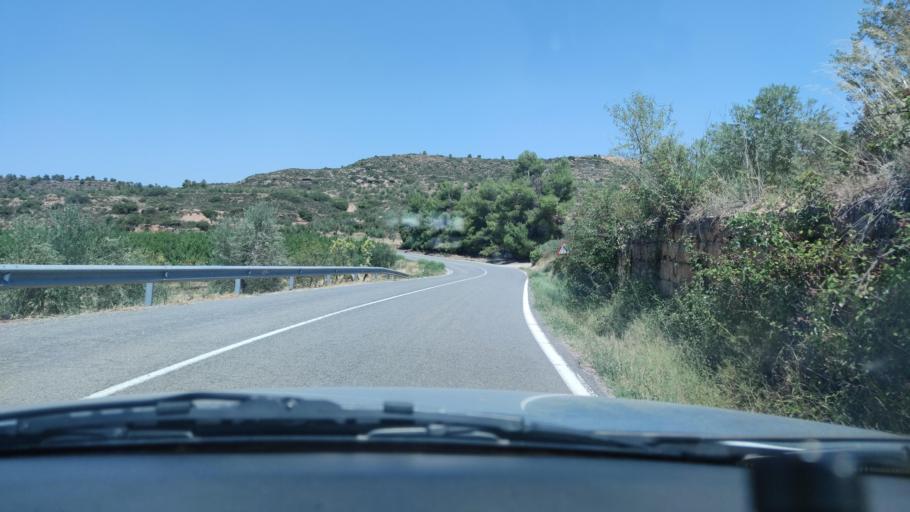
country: ES
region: Catalonia
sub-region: Provincia de Lleida
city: el Cogul
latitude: 41.4220
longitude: 0.6729
